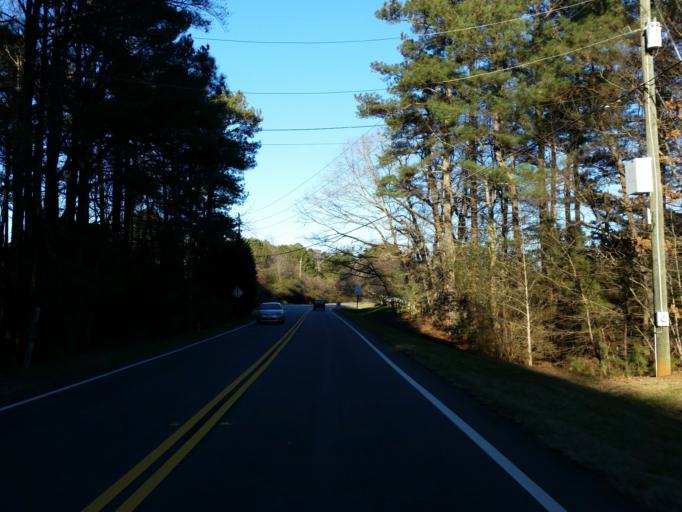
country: US
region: Georgia
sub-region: Cobb County
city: Acworth
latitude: 33.9782
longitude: -84.7023
